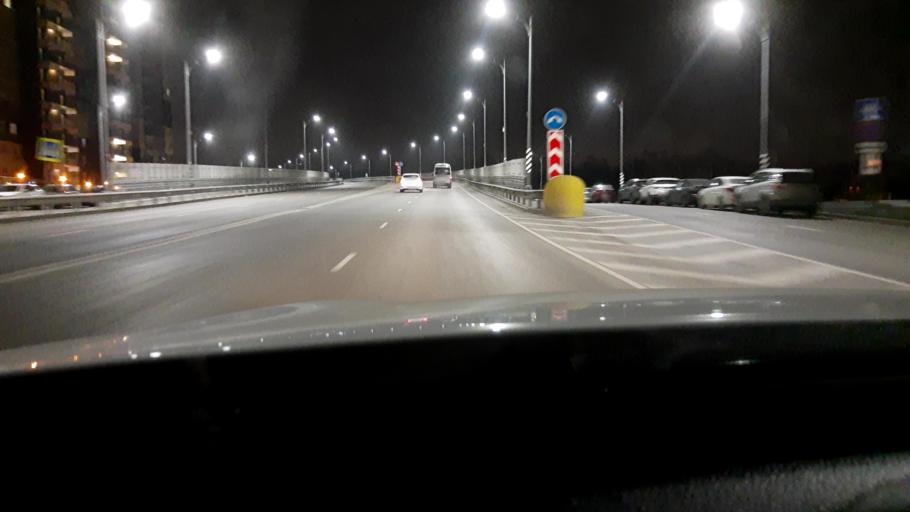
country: RU
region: Moskovskaya
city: Reutov
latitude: 55.7553
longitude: 37.8881
